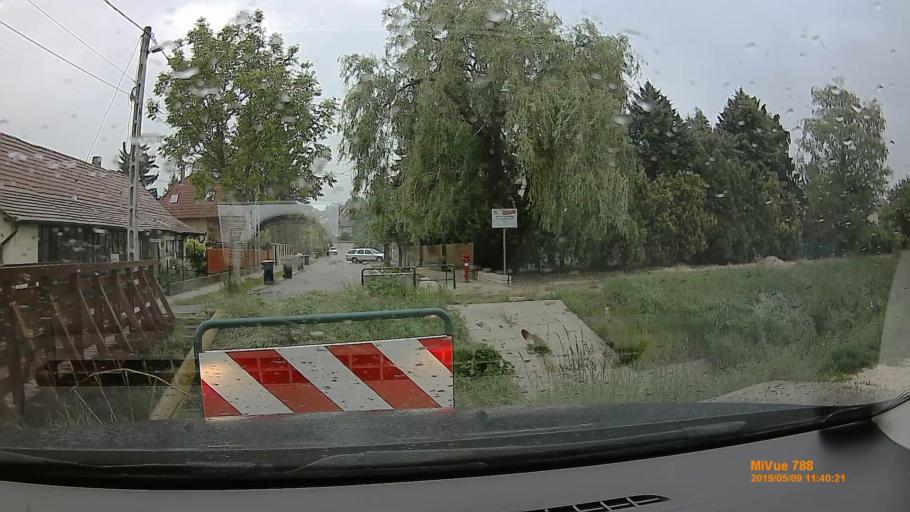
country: HU
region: Budapest
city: Budapest XVI. keruelet
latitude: 47.5319
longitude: 19.1844
